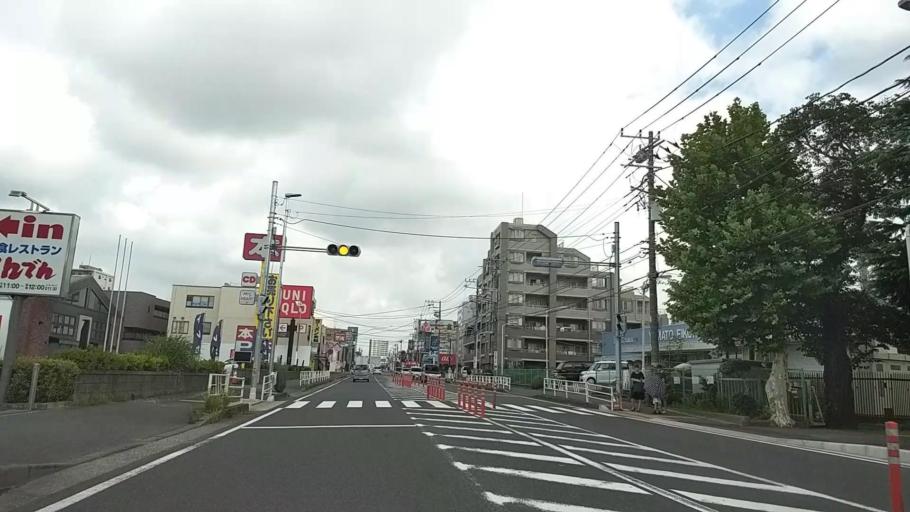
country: JP
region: Kanagawa
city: Minami-rinkan
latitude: 35.5090
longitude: 139.4611
